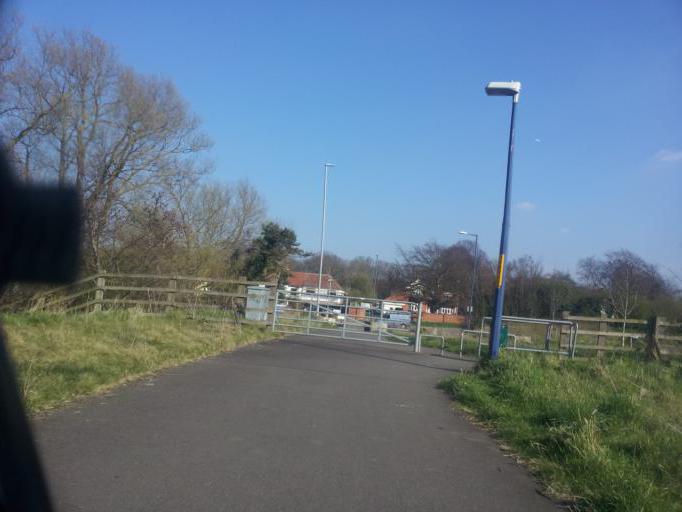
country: GB
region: England
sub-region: Kent
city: Gravesend
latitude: 51.4098
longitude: 0.3864
